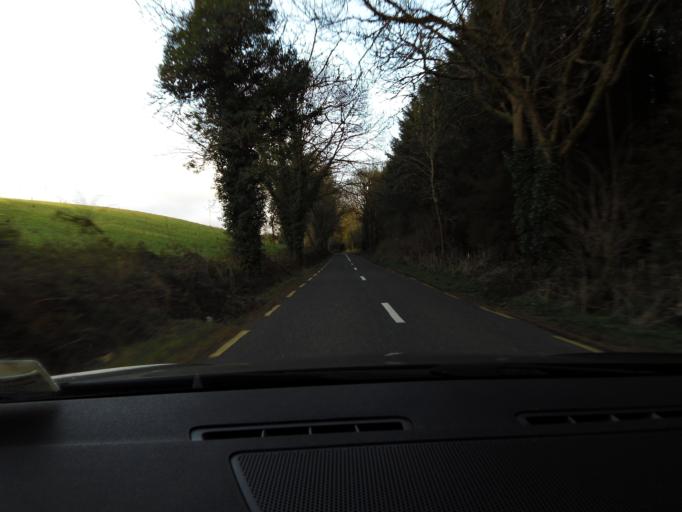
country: IE
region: Connaught
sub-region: Sligo
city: Ballymote
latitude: 54.0389
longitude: -8.6199
